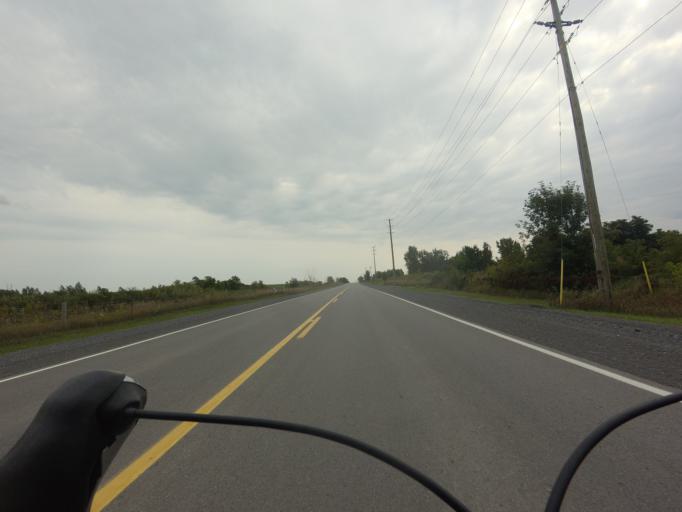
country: CA
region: Ontario
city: Bells Corners
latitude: 45.2335
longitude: -75.7818
